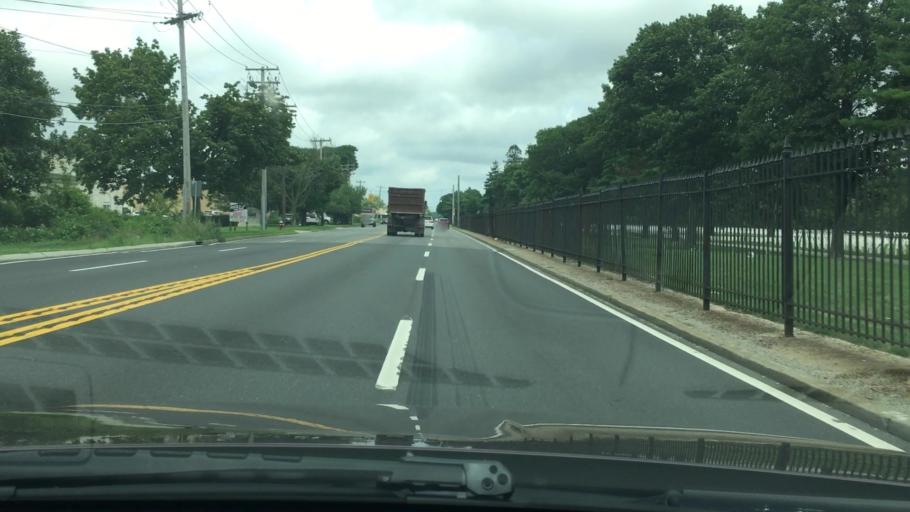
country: US
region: New York
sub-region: Suffolk County
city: East Farmingdale
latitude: 40.7520
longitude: -73.4018
